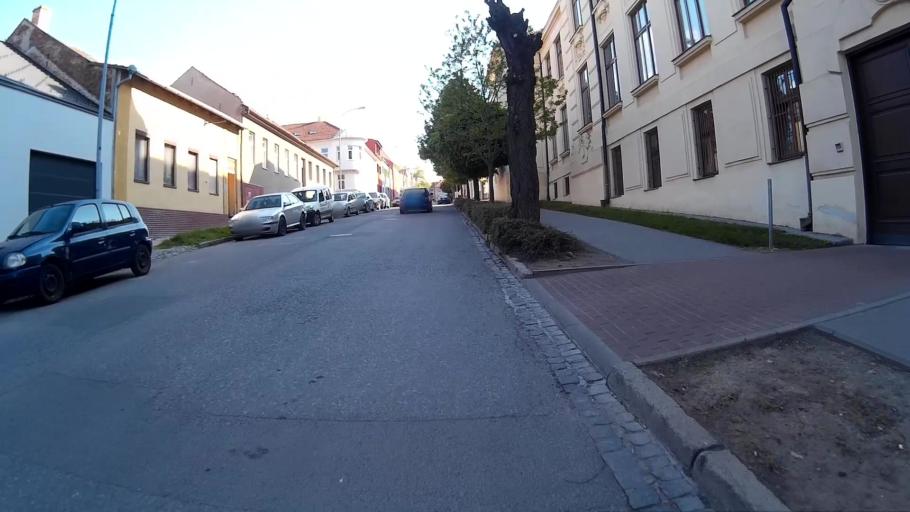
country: CZ
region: South Moravian
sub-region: Mesto Brno
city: Brno
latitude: 49.2105
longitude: 16.5826
